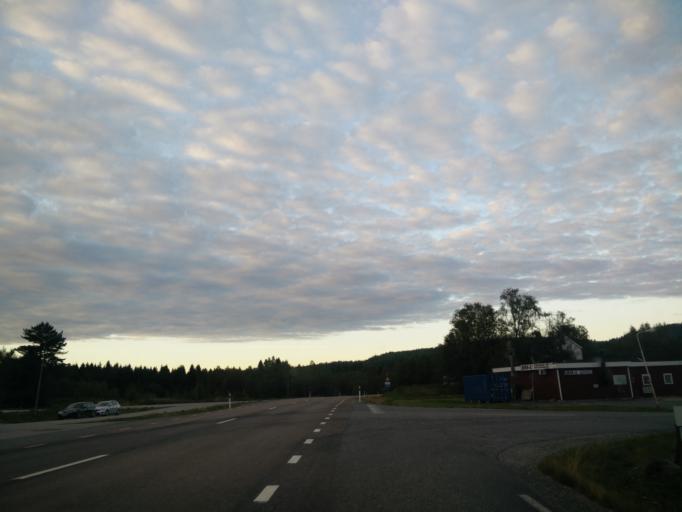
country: SE
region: Vaesternorrland
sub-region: Kramfors Kommun
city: Nordingra
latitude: 62.9298
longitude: 18.0853
